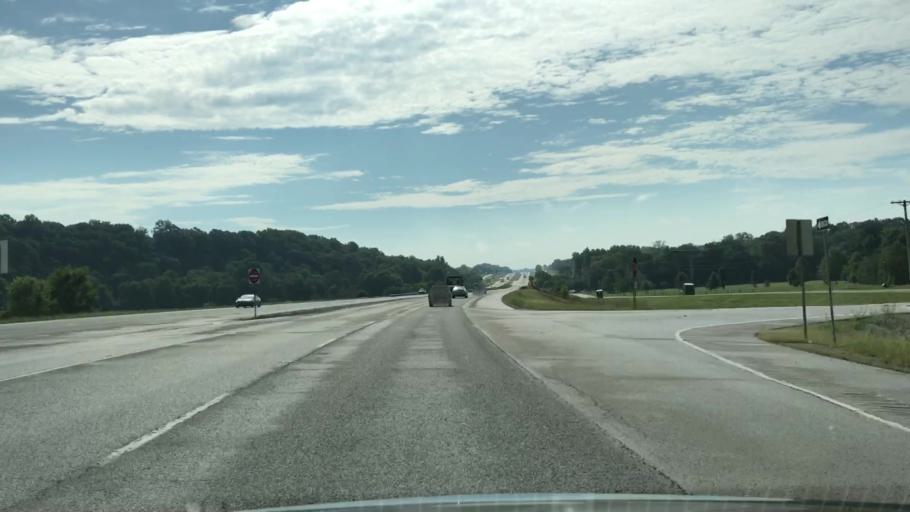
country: US
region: Kentucky
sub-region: Warren County
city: Plano
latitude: 36.8993
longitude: -86.3860
